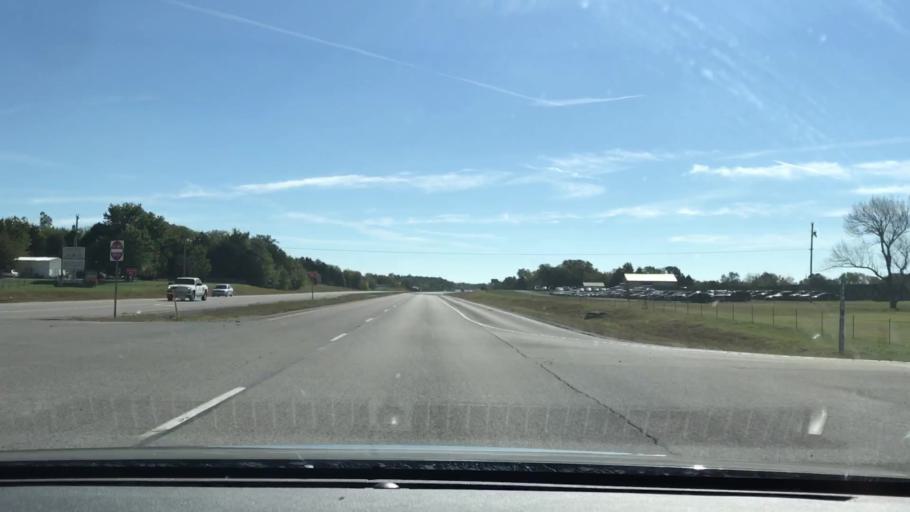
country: US
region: Kentucky
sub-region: Todd County
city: Elkton
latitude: 36.8364
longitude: -87.2381
